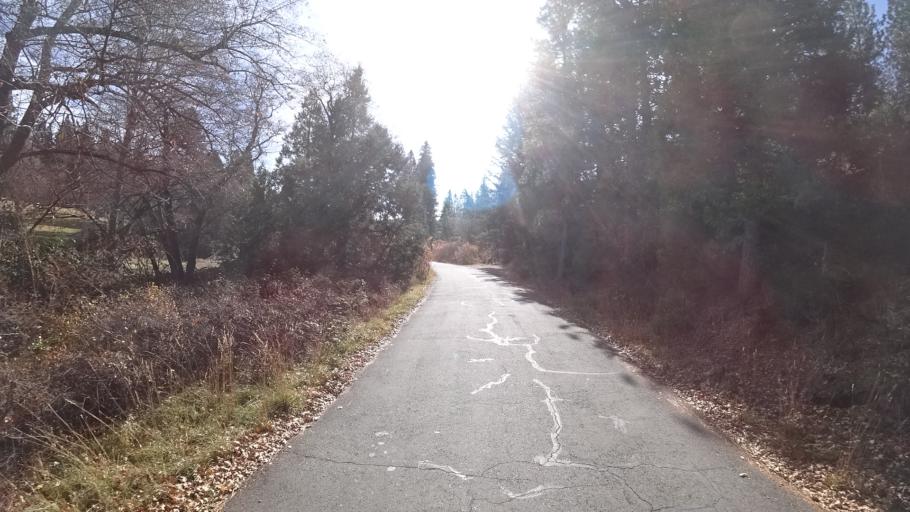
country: US
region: California
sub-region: Siskiyou County
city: Weed
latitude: 41.4299
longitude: -122.3980
